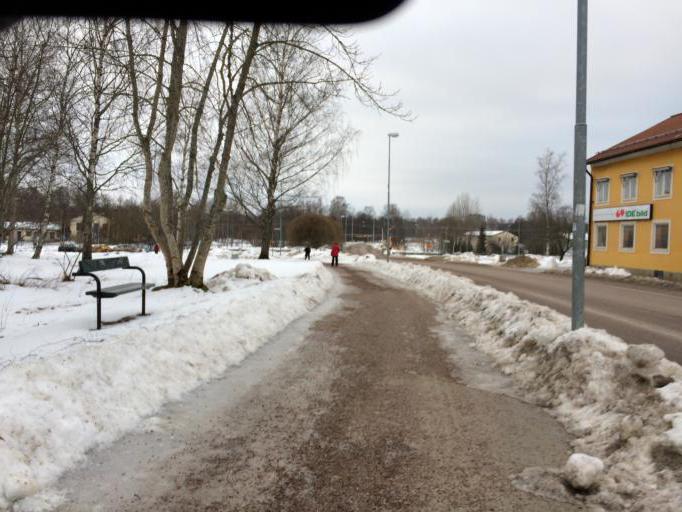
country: SE
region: Vaestmanland
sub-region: Hallstahammars Kommun
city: Hallstahammar
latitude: 59.6161
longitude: 16.2211
